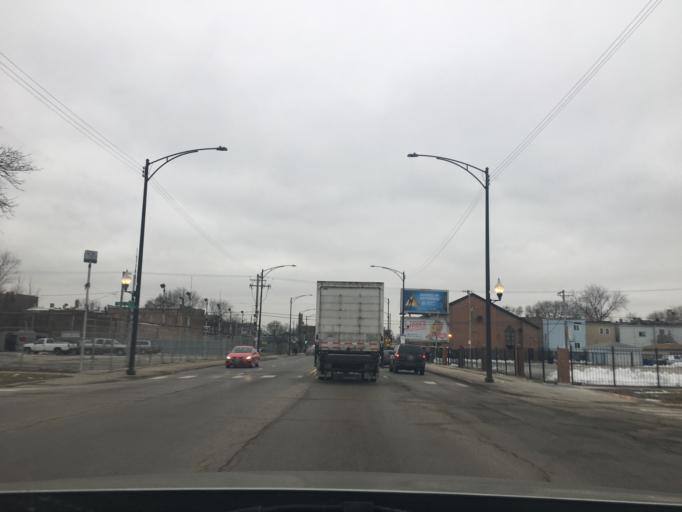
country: US
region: Illinois
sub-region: Cook County
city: Cicero
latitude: 41.8833
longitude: -87.7454
